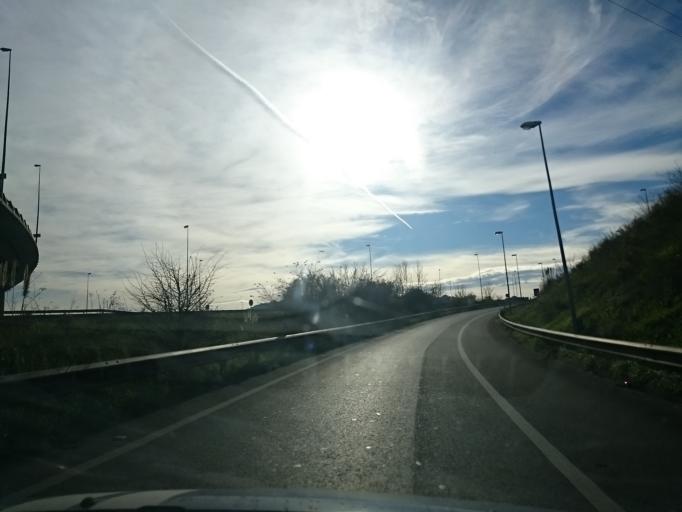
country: ES
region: Asturias
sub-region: Province of Asturias
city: Gijon
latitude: 43.5167
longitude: -5.6571
